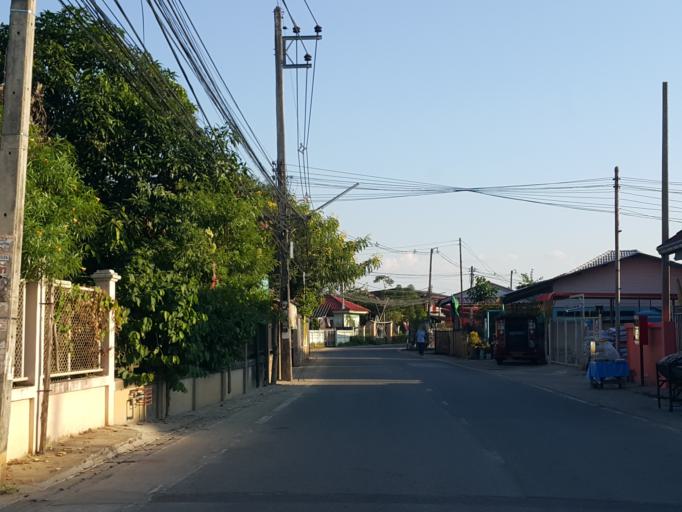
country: TH
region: Chiang Mai
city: San Sai
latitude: 18.7858
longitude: 99.0497
